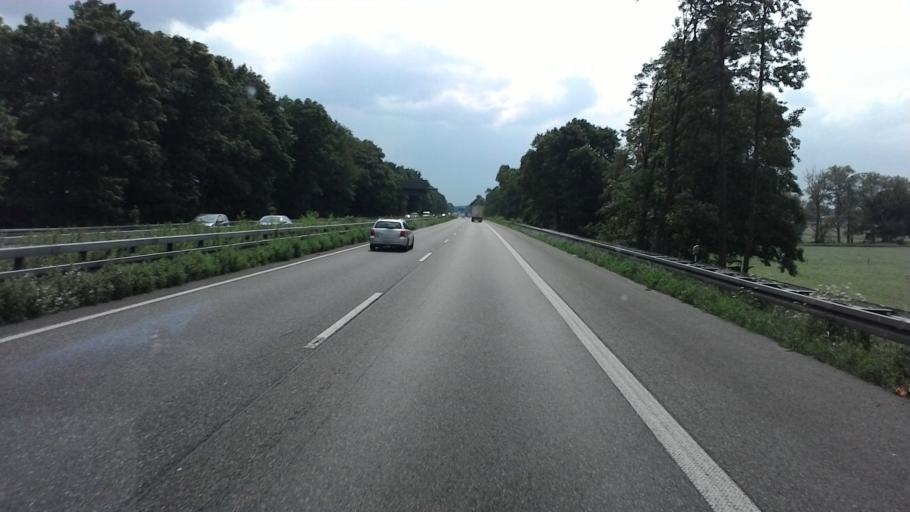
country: DE
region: North Rhine-Westphalia
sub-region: Regierungsbezirk Koln
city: Aachen
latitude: 50.7443
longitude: 6.1418
